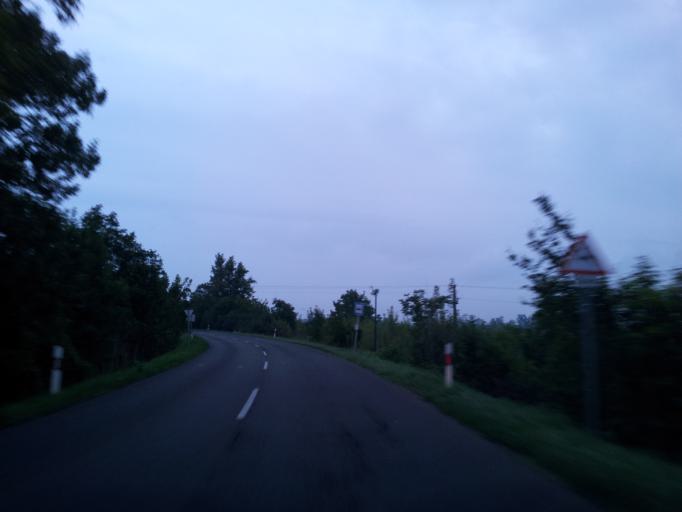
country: HU
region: Tolna
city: Fadd
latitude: 46.4500
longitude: 18.8294
